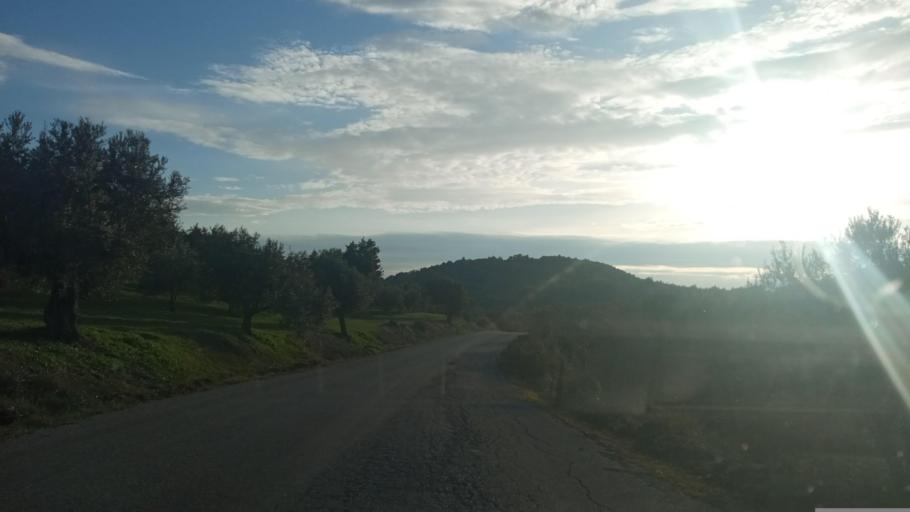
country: GR
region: Central Greece
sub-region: Nomos Evvoias
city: Psachna
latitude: 38.6086
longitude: 23.7293
